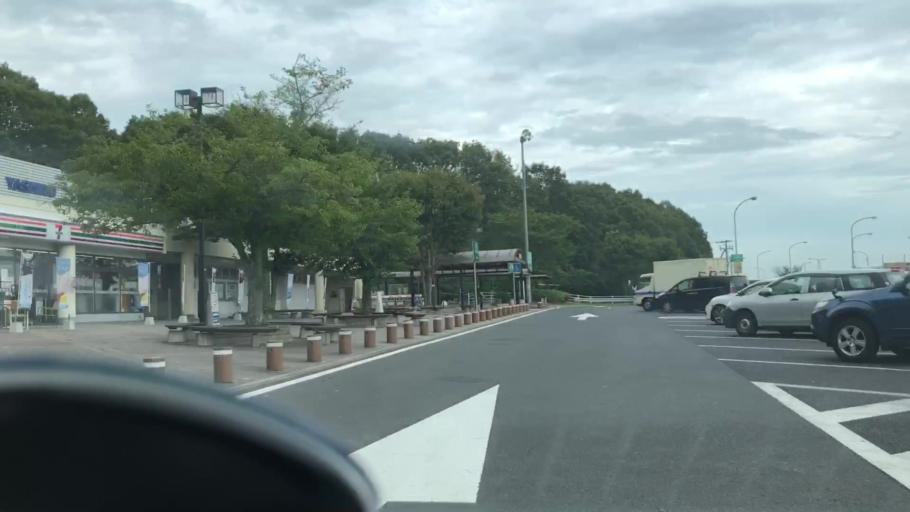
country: JP
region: Hyogo
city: Yashiro
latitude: 34.9203
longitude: 134.9996
